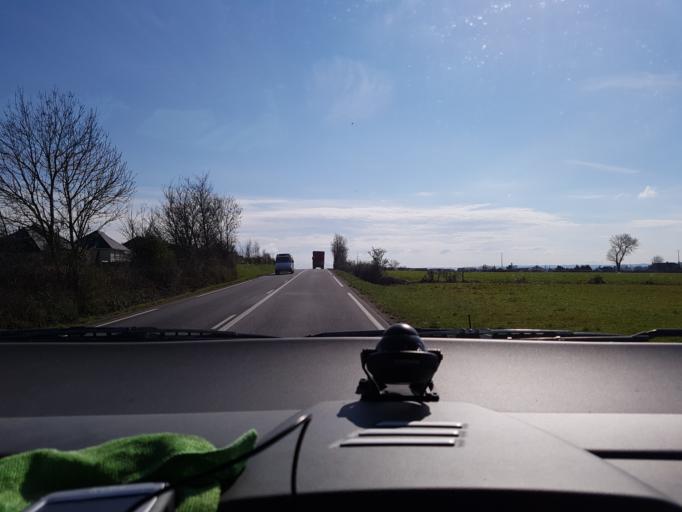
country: FR
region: Midi-Pyrenees
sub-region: Departement de l'Aveyron
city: Druelle
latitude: 44.3692
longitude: 2.5109
